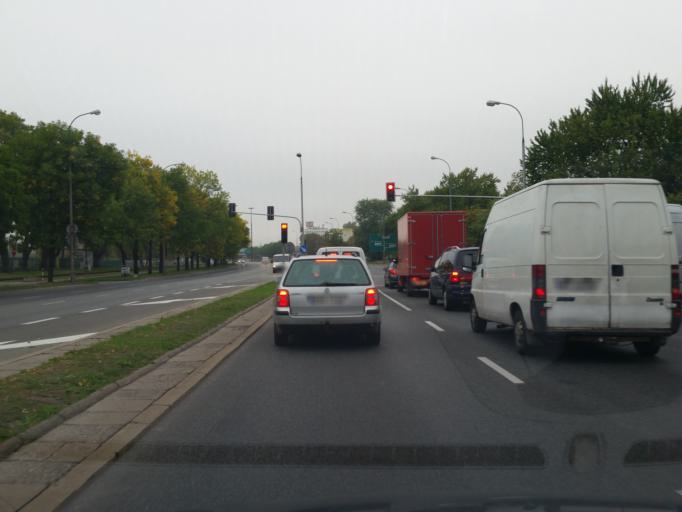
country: PL
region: Masovian Voivodeship
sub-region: Warszawa
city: Zoliborz
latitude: 52.2846
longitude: 21.0083
